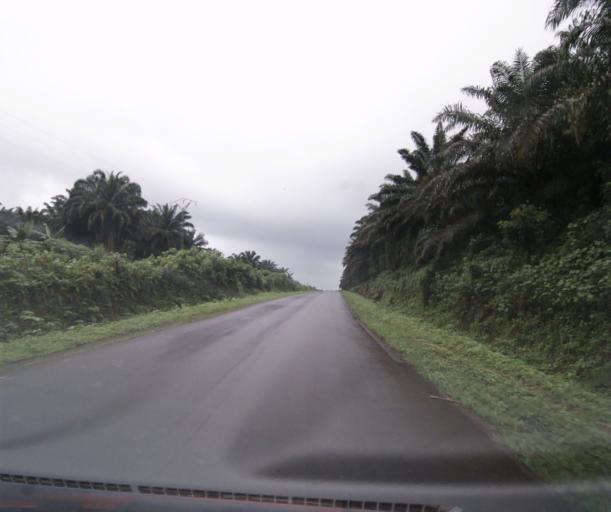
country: CM
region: South-West Province
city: Idenao
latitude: 4.1386
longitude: 8.9903
